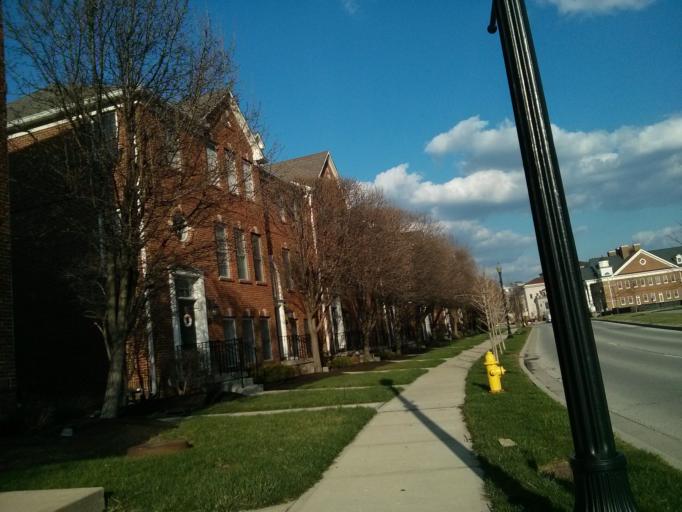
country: US
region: Indiana
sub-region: Hamilton County
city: Carmel
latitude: 39.9708
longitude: -86.1347
